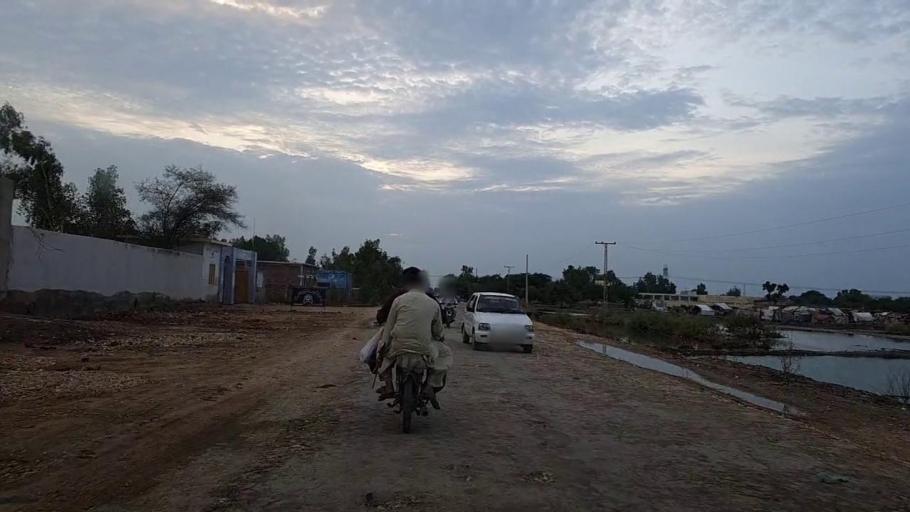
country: PK
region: Sindh
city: Naushahro Firoz
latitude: 26.8289
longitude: 68.1447
